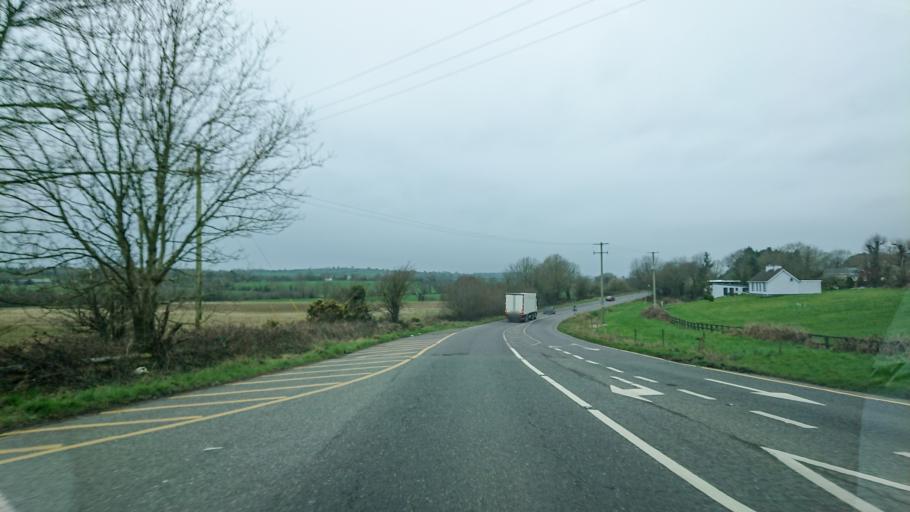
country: IE
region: Munster
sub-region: County Cork
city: Bandon
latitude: 51.7431
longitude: -8.8111
